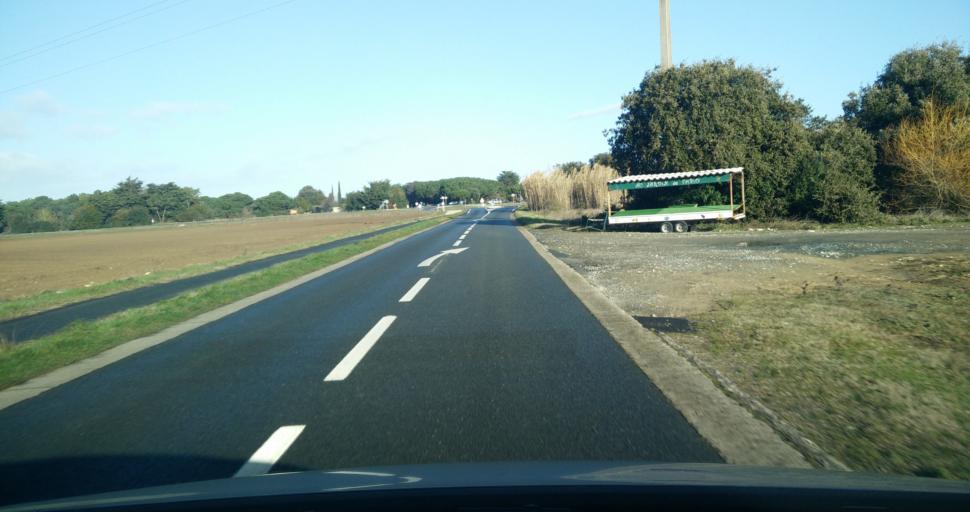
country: FR
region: Poitou-Charentes
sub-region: Departement de la Charente-Maritime
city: La Flotte
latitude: 46.1768
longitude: -1.3319
